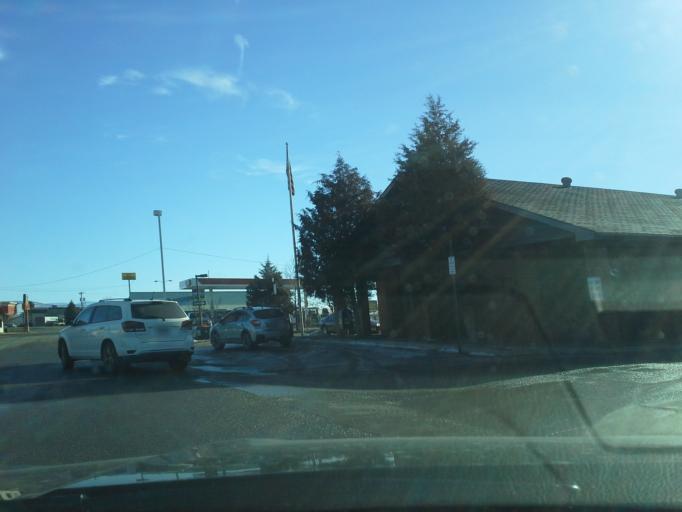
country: US
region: Montana
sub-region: Lewis and Clark County
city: East Helena
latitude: 46.5877
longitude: -111.9110
